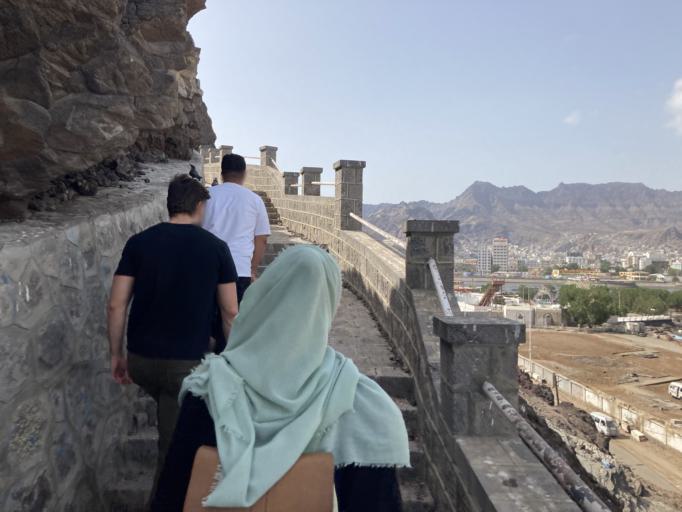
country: YE
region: Aden
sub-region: Craiter
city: Aden
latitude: 12.7816
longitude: 45.0497
